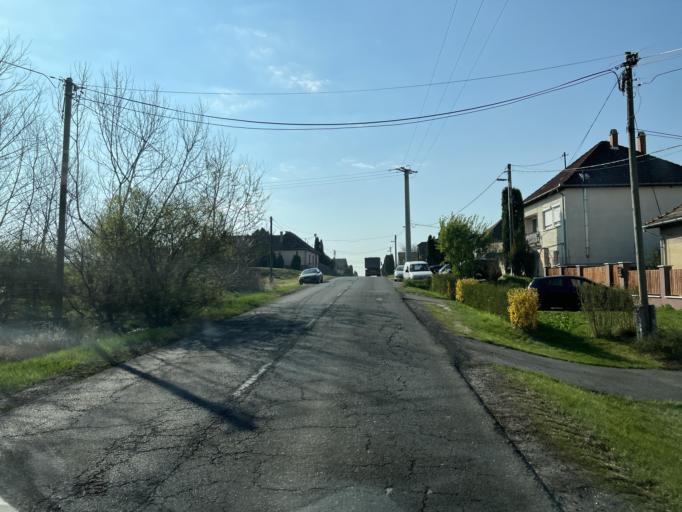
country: HU
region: Pest
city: Galgamacsa
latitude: 47.7032
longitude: 19.3949
